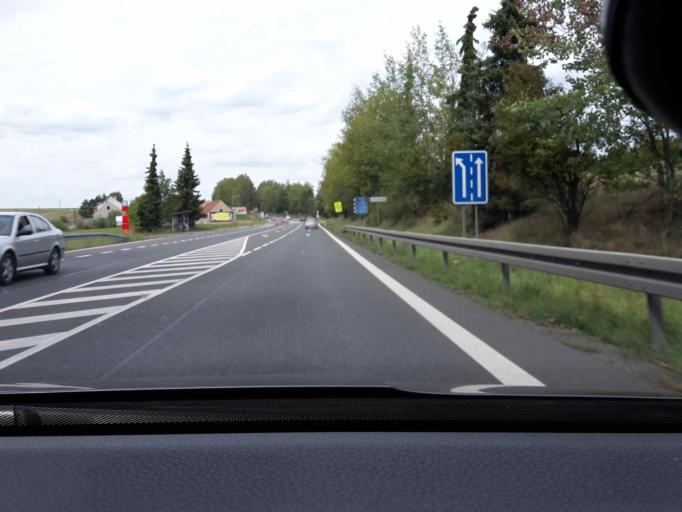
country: CZ
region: Central Bohemia
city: Bystrice
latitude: 49.7538
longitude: 14.6727
